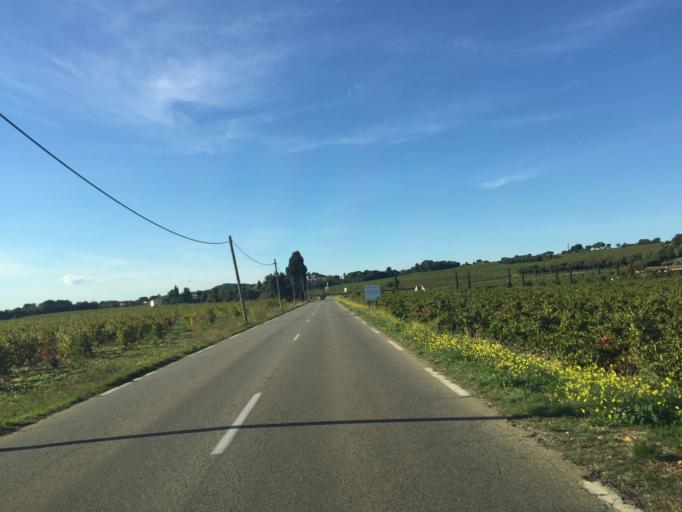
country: FR
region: Provence-Alpes-Cote d'Azur
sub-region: Departement du Vaucluse
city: Chateauneuf-du-Pape
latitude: 44.0448
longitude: 4.8468
